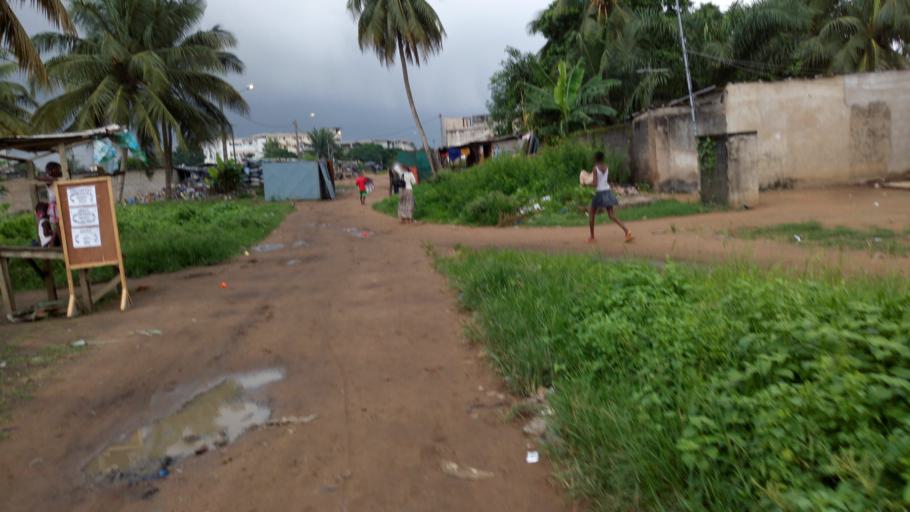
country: CI
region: Lagunes
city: Abobo
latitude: 5.4069
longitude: -3.9975
